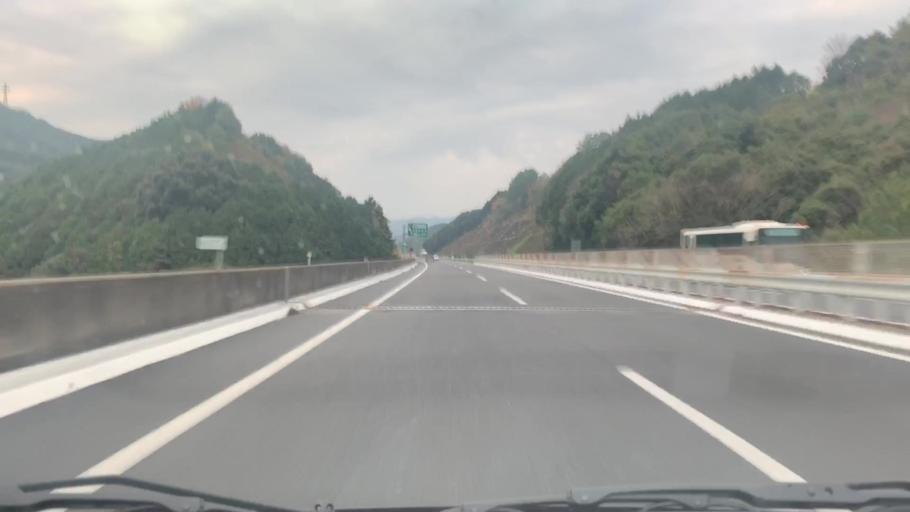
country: JP
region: Nagasaki
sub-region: Isahaya-shi
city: Isahaya
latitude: 32.8189
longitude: 129.9801
